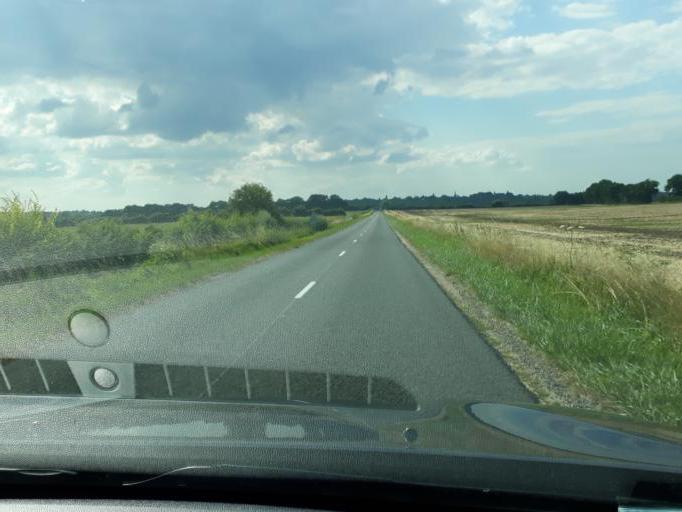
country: FR
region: Centre
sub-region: Departement du Cher
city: Nerondes
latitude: 47.0573
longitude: 2.8308
